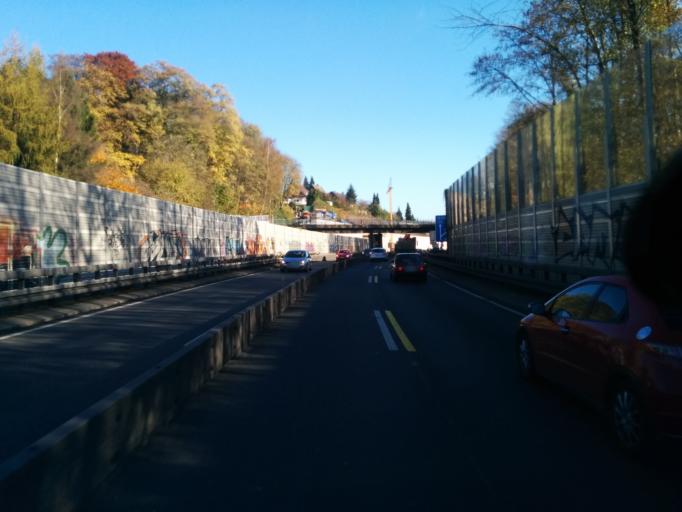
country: DE
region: North Rhine-Westphalia
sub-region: Regierungsbezirk Dusseldorf
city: Wuppertal
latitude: 51.2613
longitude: 7.1150
